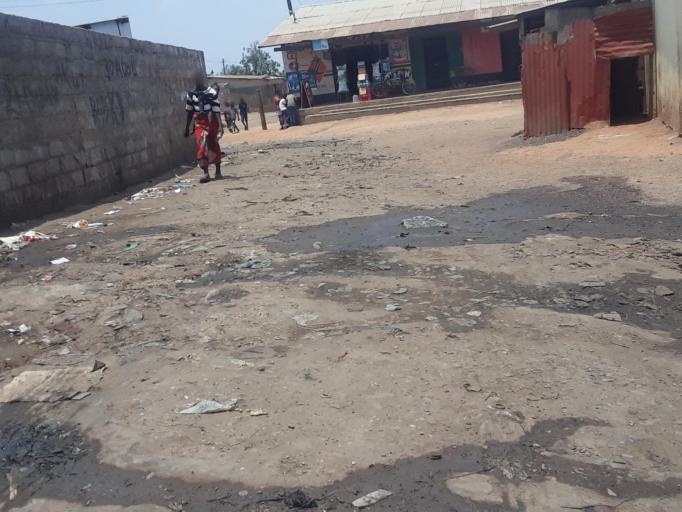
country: ZM
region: Lusaka
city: Lusaka
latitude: -15.3647
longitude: 28.2995
